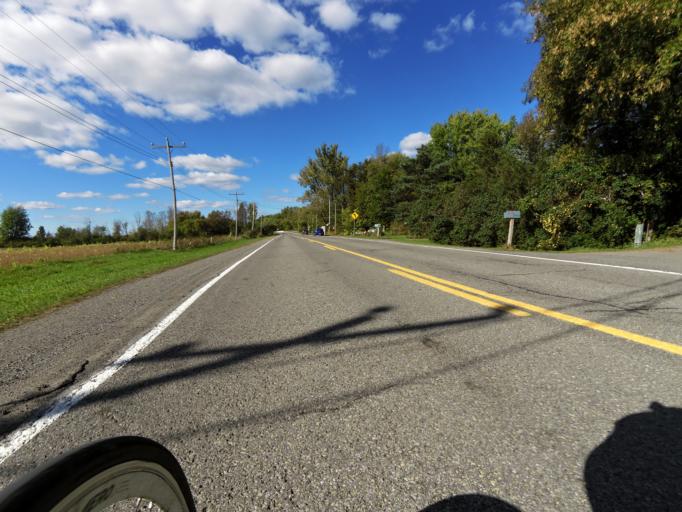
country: CA
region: Ontario
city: Bells Corners
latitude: 45.1360
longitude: -75.6406
